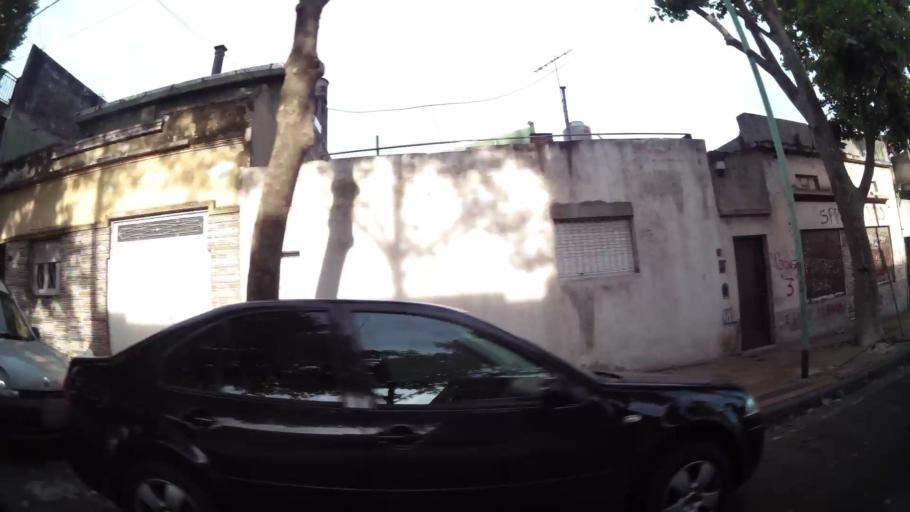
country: AR
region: Buenos Aires F.D.
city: Villa Lugano
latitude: -34.6442
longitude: -58.4278
